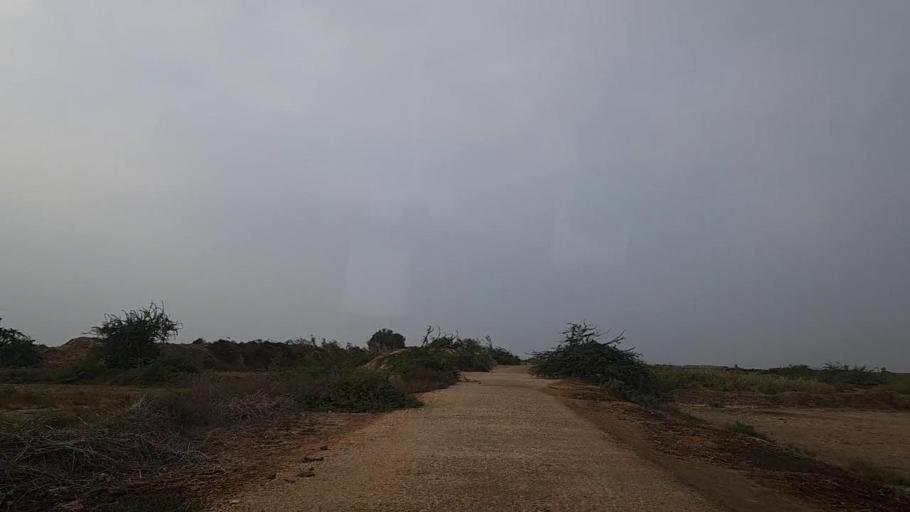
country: PK
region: Sindh
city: Mirpur Sakro
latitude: 24.6087
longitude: 67.5157
